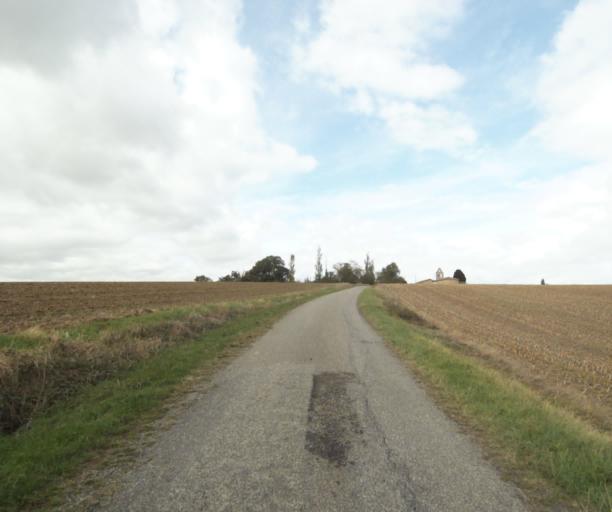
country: FR
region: Midi-Pyrenees
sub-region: Departement du Tarn-et-Garonne
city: Beaumont-de-Lomagne
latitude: 43.8764
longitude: 1.0833
